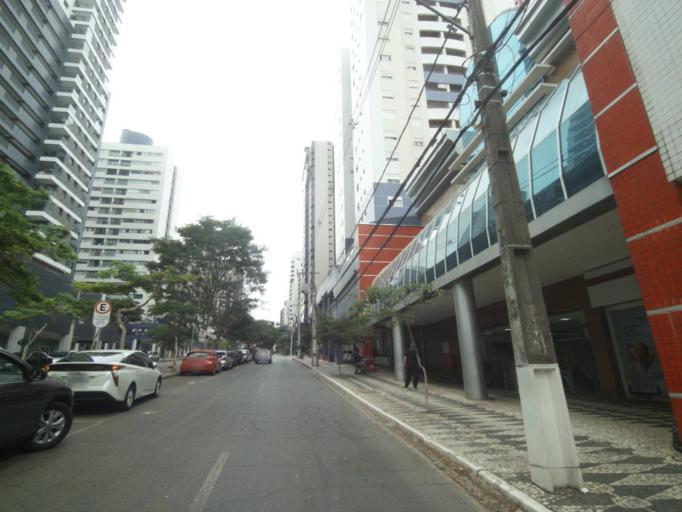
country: BR
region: Parana
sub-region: Curitiba
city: Curitiba
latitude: -25.4349
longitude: -49.3039
